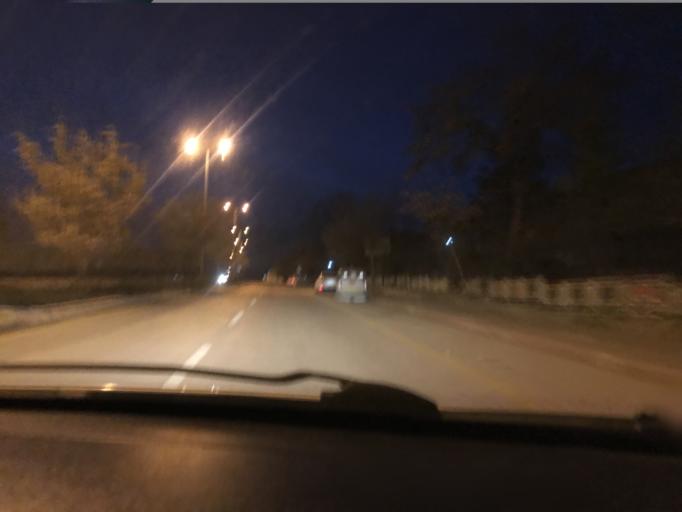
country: TR
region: Ankara
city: Batikent
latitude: 39.9599
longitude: 32.7448
